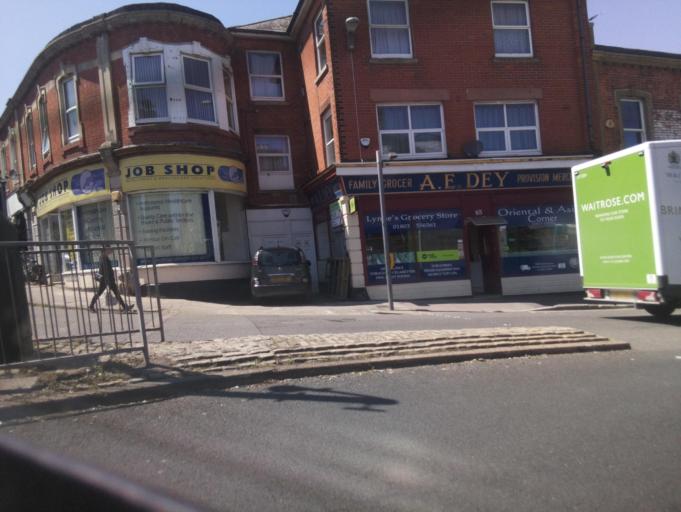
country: GB
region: England
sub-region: Borough of Torbay
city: Paignton
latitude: 50.4378
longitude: -3.5677
